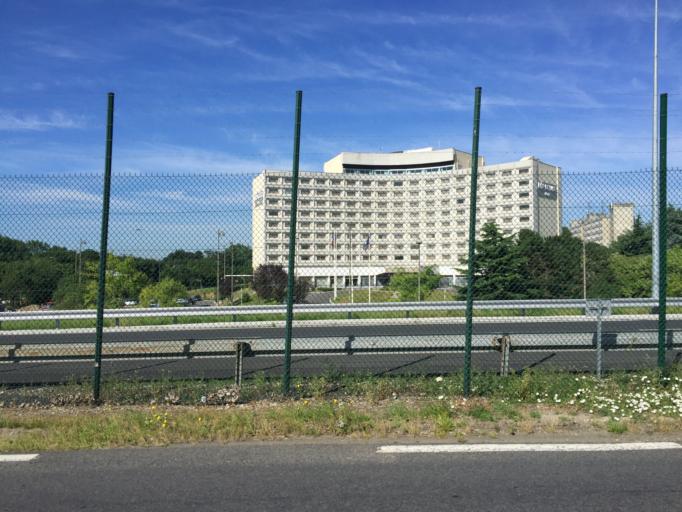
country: FR
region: Ile-de-France
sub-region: Departement du Val-d'Oise
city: Roissy-en-France
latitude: 49.0077
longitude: 2.5509
